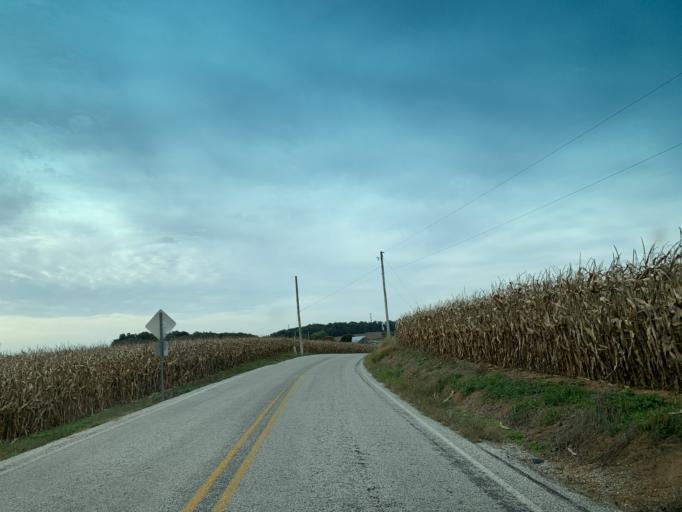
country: US
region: Pennsylvania
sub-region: York County
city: Stewartstown
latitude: 39.8053
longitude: -76.4916
